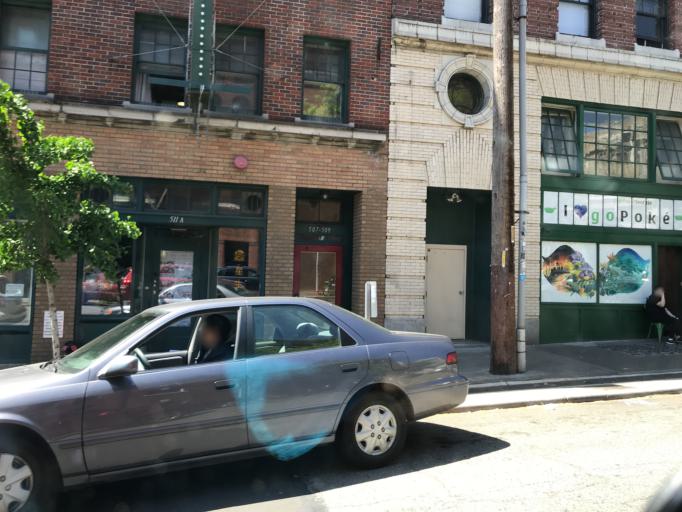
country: US
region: Washington
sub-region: King County
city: Seattle
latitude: 47.5980
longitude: -122.3251
